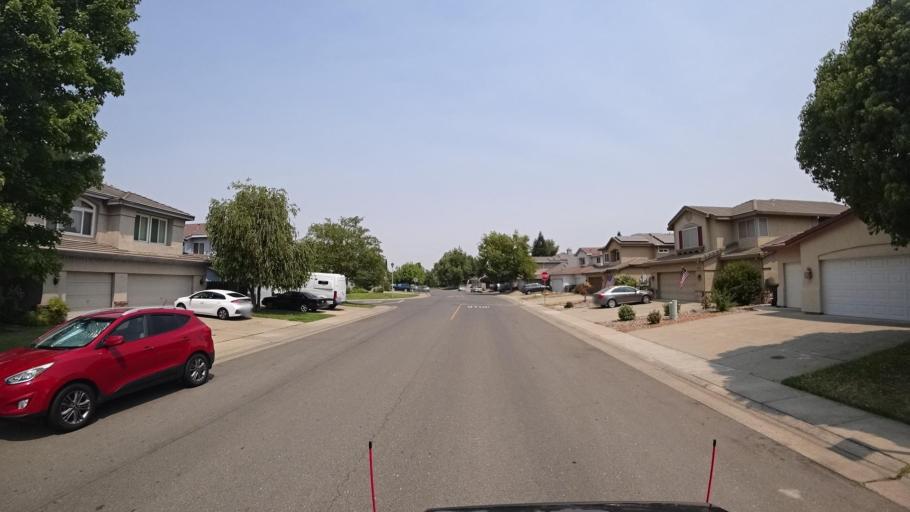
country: US
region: California
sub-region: Placer County
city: Rocklin
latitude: 38.8017
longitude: -121.2661
